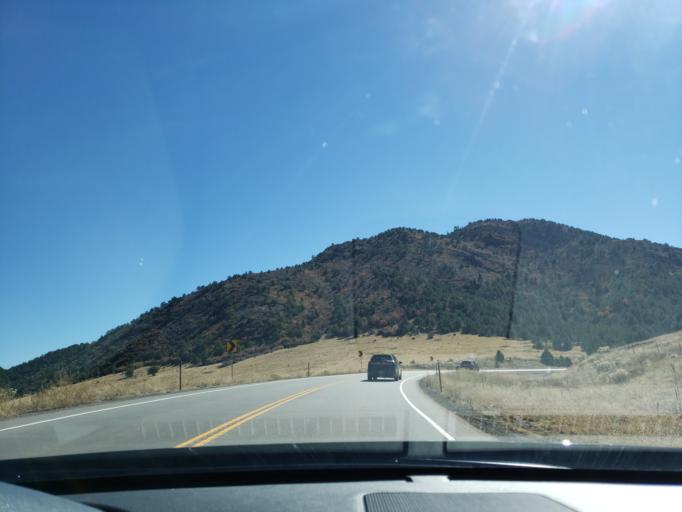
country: US
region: Colorado
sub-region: Fremont County
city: Canon City
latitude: 38.5836
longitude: -105.4158
